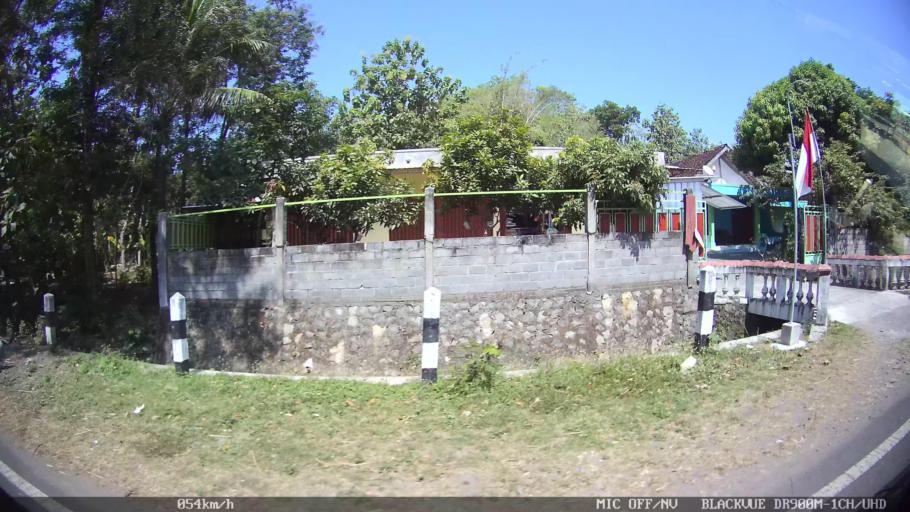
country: ID
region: Daerah Istimewa Yogyakarta
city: Pundong
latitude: -7.9622
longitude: 110.3563
